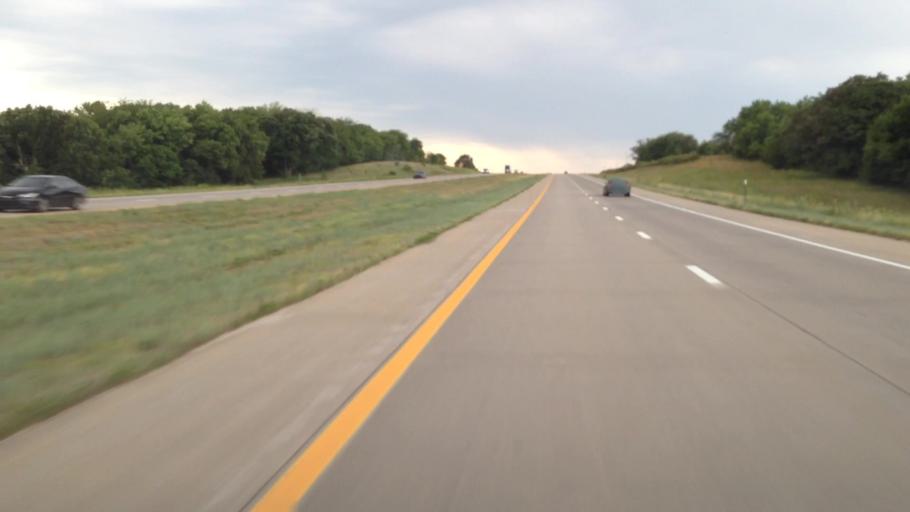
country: US
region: Kansas
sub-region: Osage County
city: Lyndon
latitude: 38.4801
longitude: -95.5011
